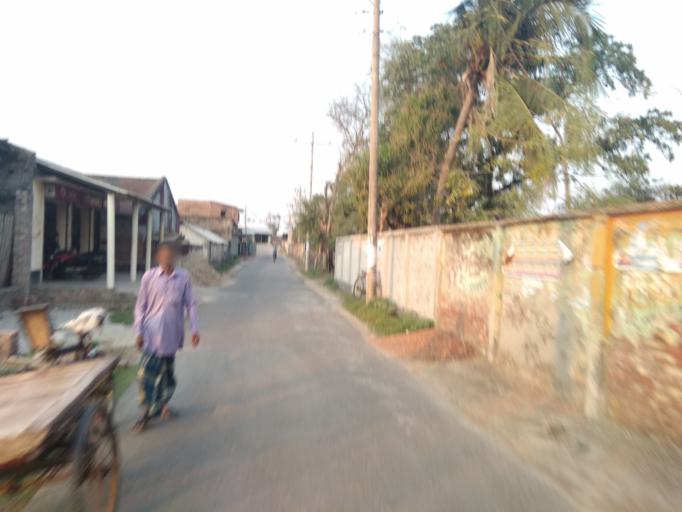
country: BD
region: Khulna
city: Satkhira
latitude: 22.5474
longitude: 89.1734
